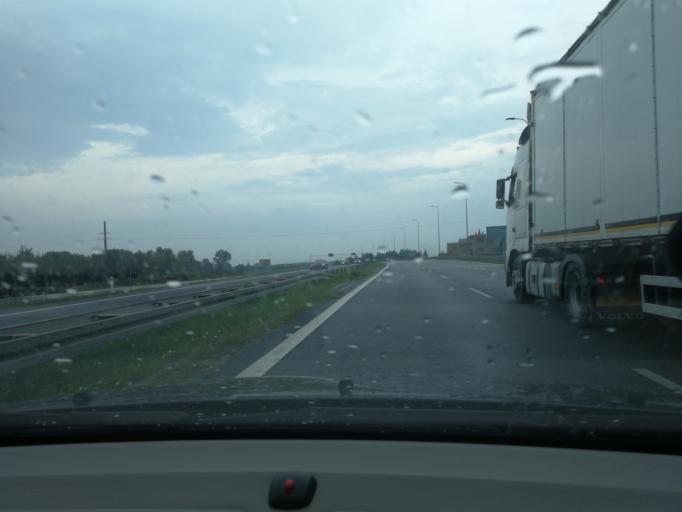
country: PL
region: Masovian Voivodeship
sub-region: Powiat zyrardowski
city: Mszczonow
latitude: 51.9839
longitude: 20.5291
